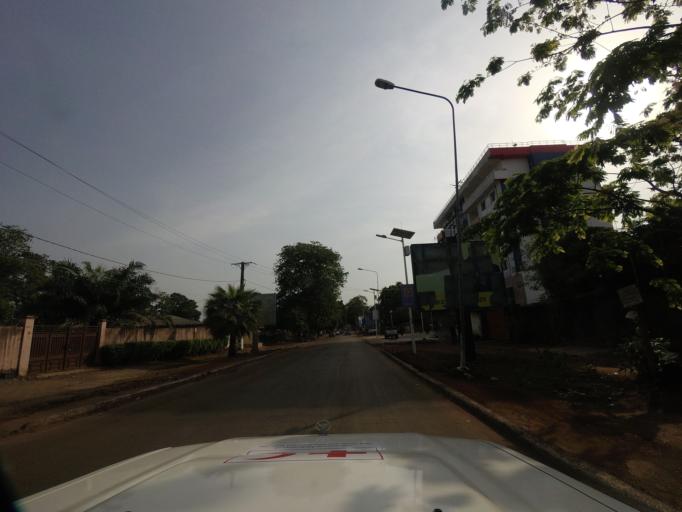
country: GN
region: Conakry
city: Conakry
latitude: 9.5392
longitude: -13.6825
